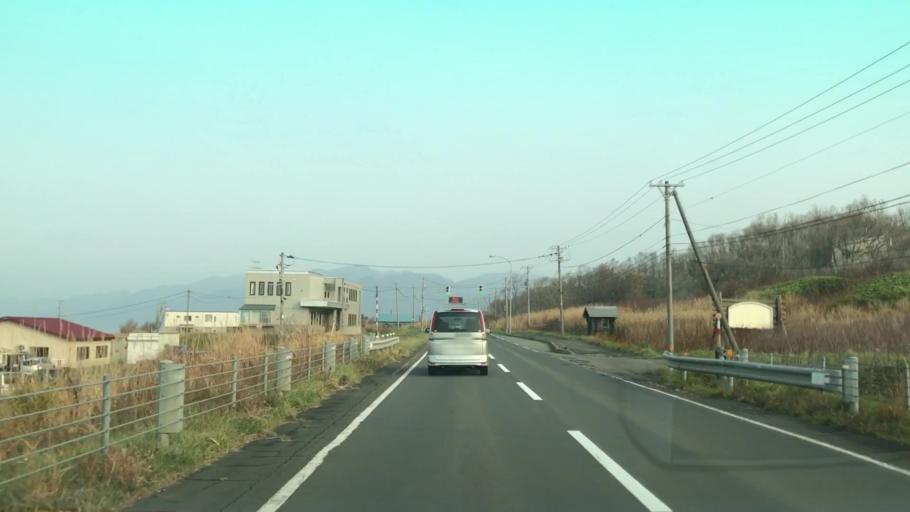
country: JP
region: Hokkaido
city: Ishikari
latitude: 43.3750
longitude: 141.4276
